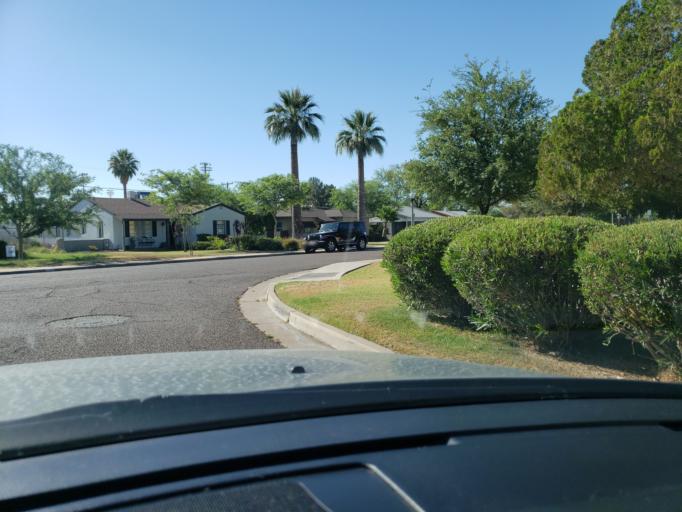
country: US
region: Arizona
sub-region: Maricopa County
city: Phoenix
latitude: 33.4794
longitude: -112.0608
